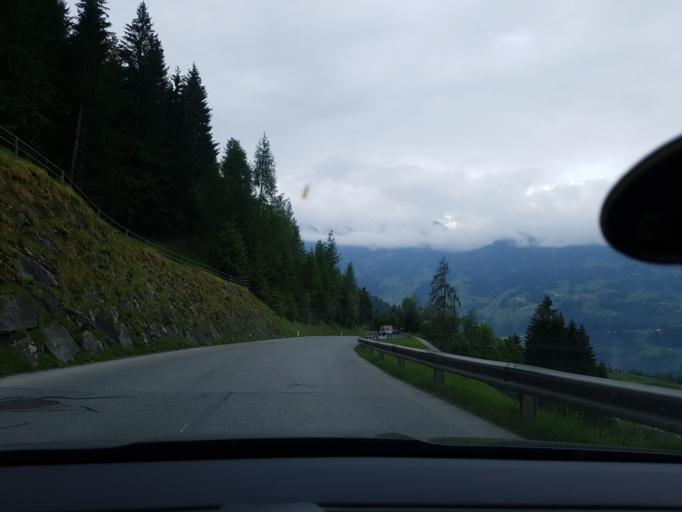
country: AT
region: Tyrol
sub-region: Politischer Bezirk Schwaz
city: Hainzenberg
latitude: 47.2146
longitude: 11.9125
